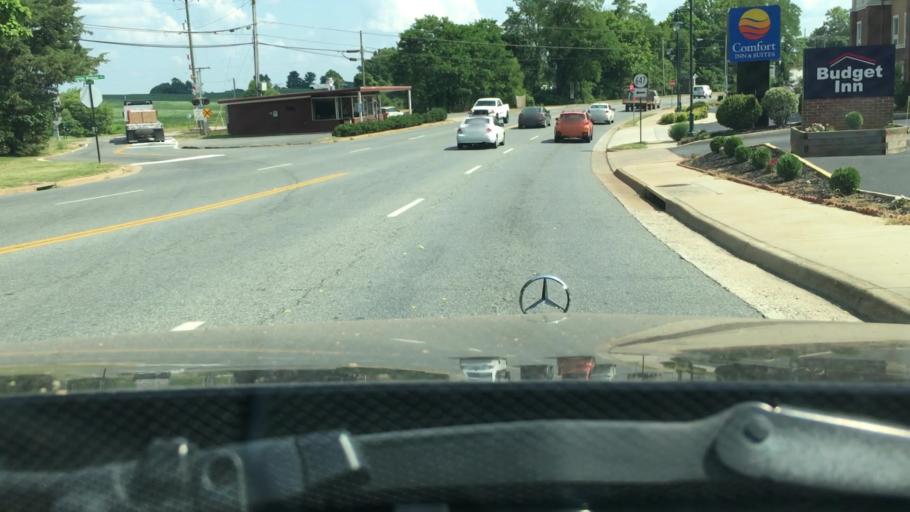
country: US
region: Virginia
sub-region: Orange County
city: Orange
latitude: 38.2364
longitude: -78.1115
